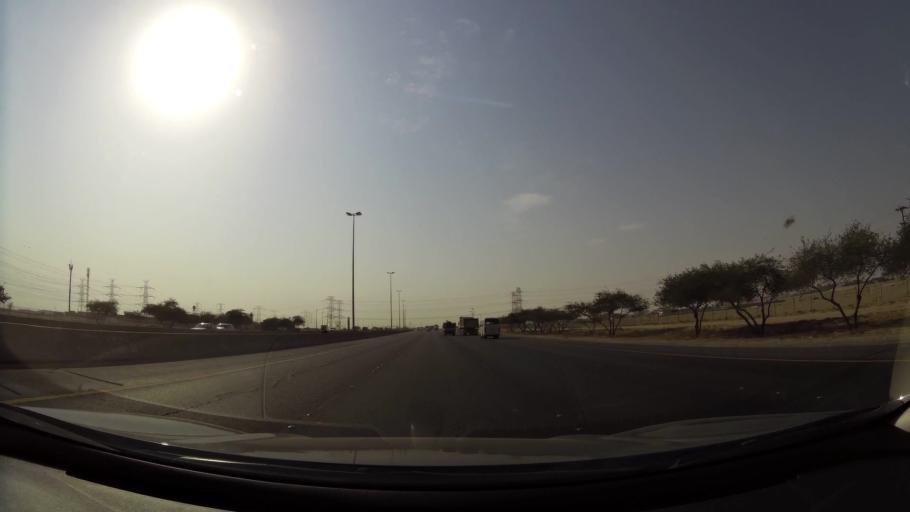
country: KW
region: Al Ahmadi
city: Al Ahmadi
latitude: 29.0093
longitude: 48.0938
